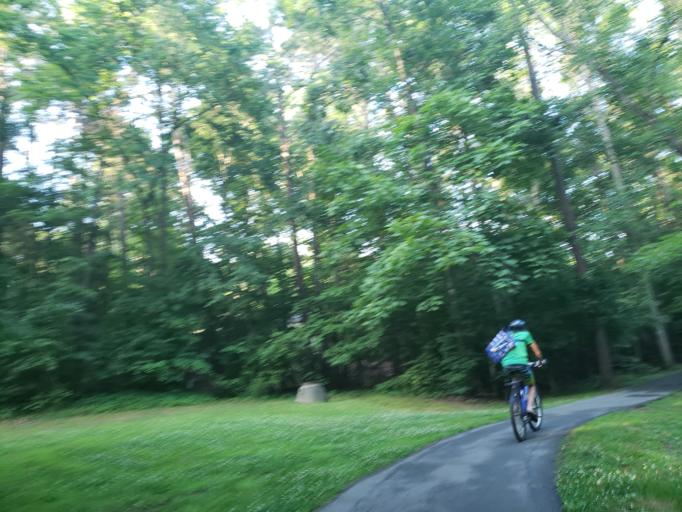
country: US
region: North Carolina
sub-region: Durham County
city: Durham
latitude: 35.9198
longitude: -78.9489
